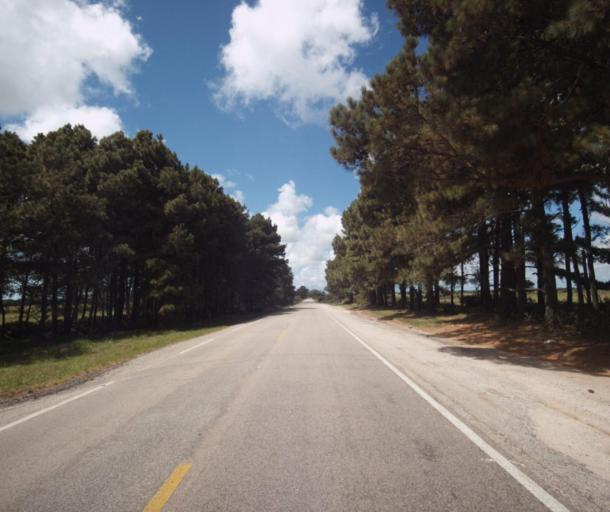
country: BR
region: Rio Grande do Sul
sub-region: Arroio Grande
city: Arroio Grande
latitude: -32.5277
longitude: -52.5448
